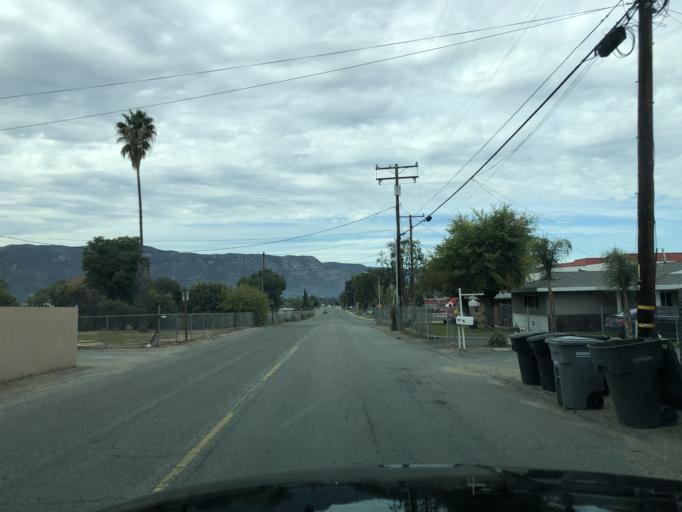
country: US
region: California
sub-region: Riverside County
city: Sedco Hills
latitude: 33.6233
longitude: -117.2769
